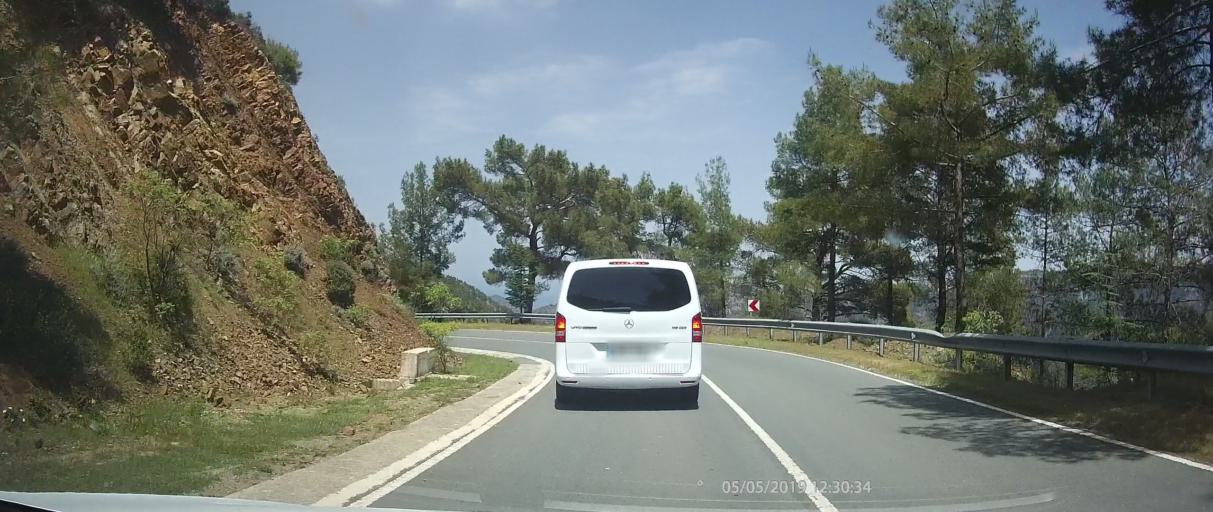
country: CY
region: Lefkosia
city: Kakopetria
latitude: 34.9847
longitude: 32.7491
